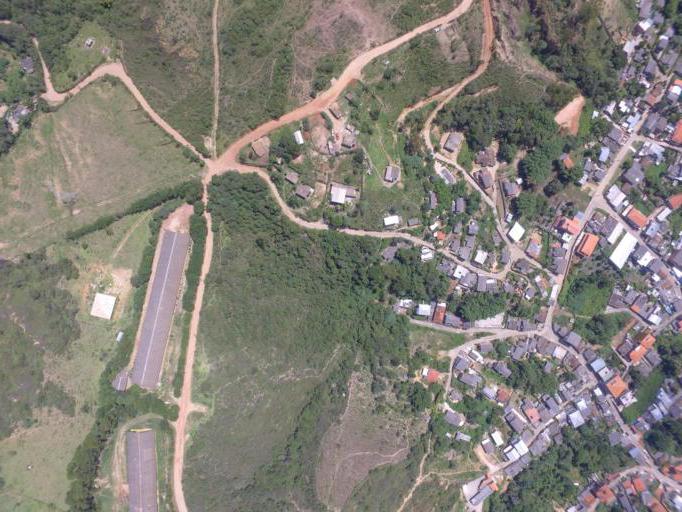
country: BR
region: Minas Gerais
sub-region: Tiradentes
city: Tiradentes
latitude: -21.0510
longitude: -44.0764
